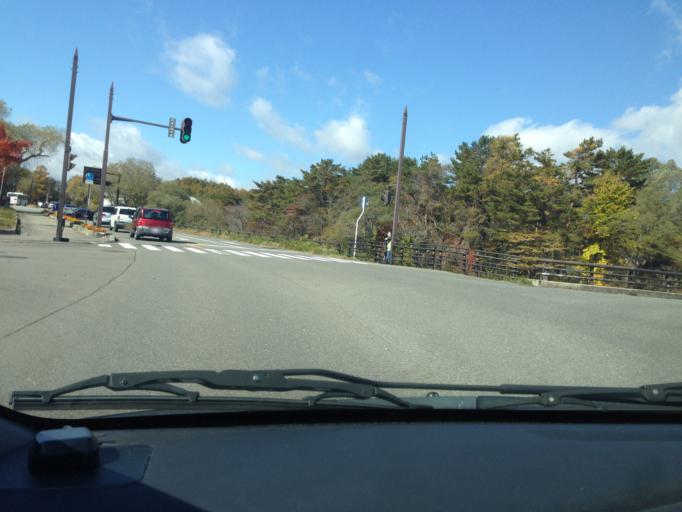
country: JP
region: Fukushima
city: Inawashiro
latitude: 37.6562
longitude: 140.0921
